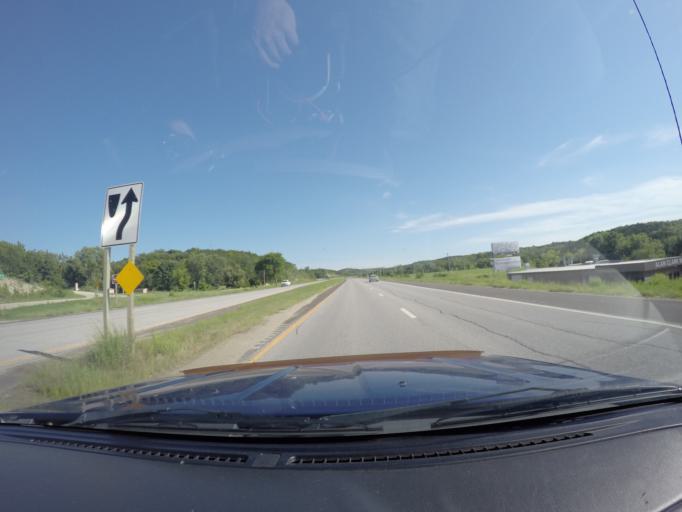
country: US
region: Kansas
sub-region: Riley County
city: Manhattan
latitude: 39.1656
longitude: -96.5404
